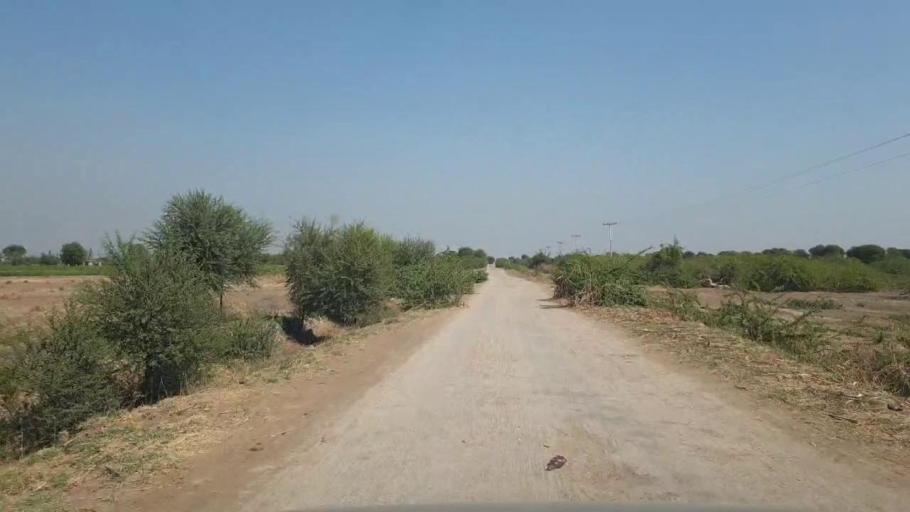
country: PK
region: Sindh
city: Digri
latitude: 25.0940
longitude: 69.2423
